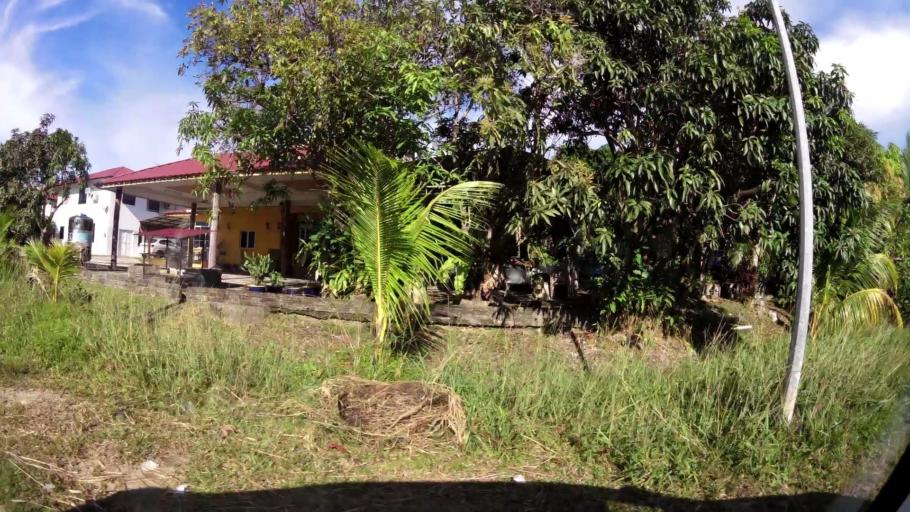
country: BN
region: Brunei and Muara
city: Bandar Seri Begawan
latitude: 4.9788
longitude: 114.9720
